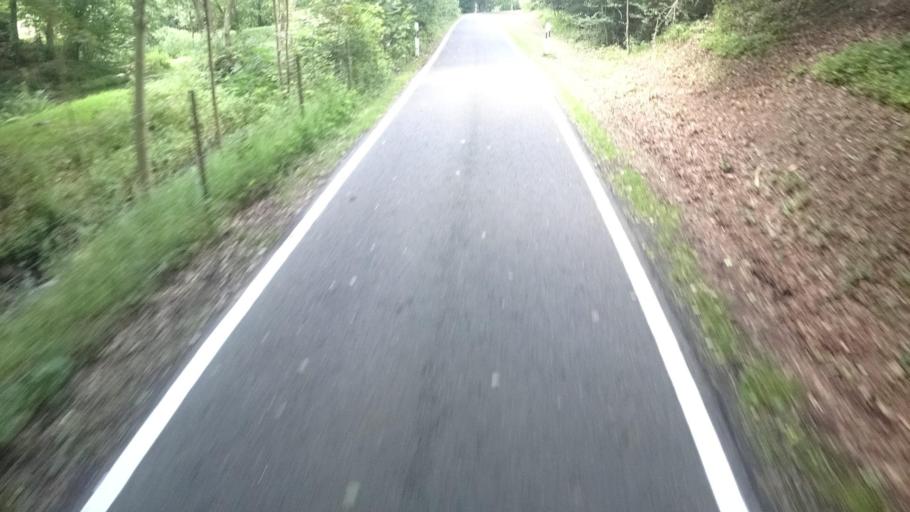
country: DE
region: Rheinland-Pfalz
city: Sankt Katharinen
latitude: 50.5765
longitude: 7.3591
